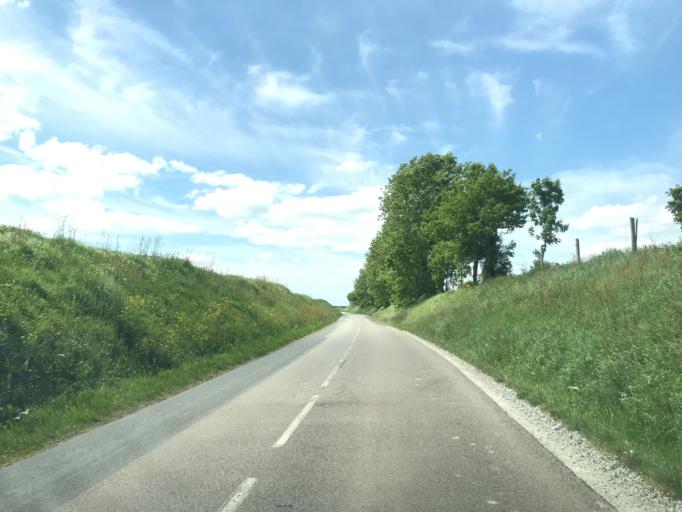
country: FR
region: Haute-Normandie
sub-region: Departement de l'Eure
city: Le Neubourg
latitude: 49.1480
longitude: 0.8924
